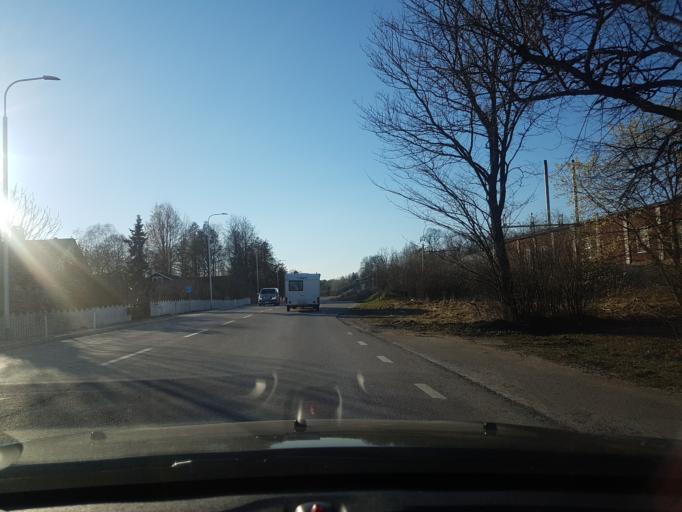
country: SE
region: Uppsala
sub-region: Heby Kommun
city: Morgongava
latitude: 59.9336
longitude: 16.9557
